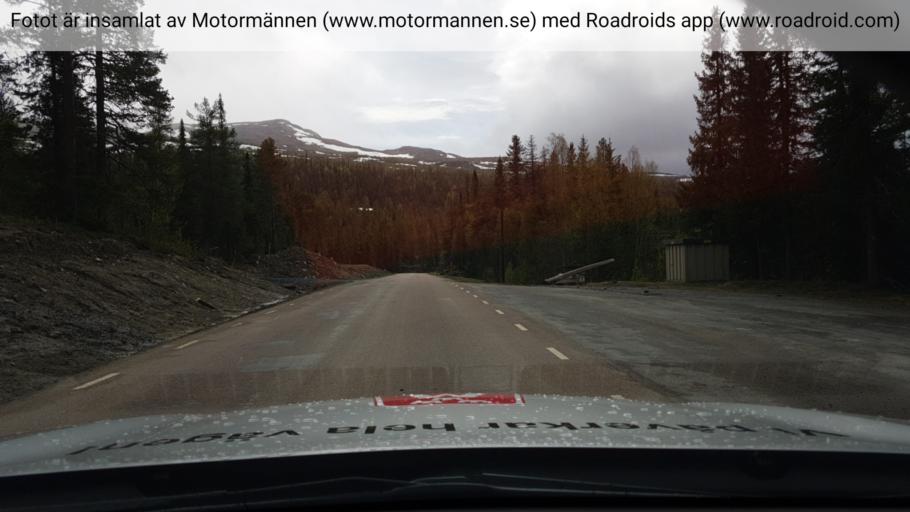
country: SE
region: Jaemtland
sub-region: Are Kommun
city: Jarpen
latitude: 63.0837
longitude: 13.7733
